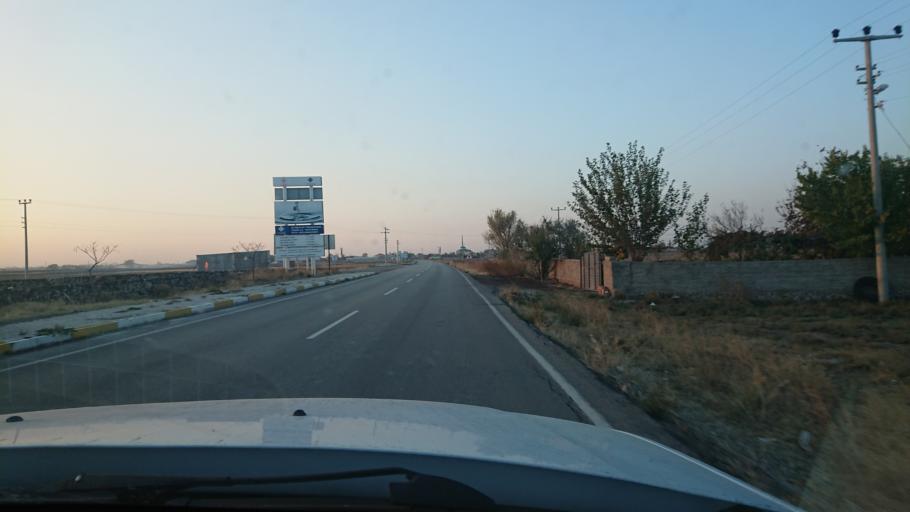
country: TR
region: Aksaray
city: Aksaray
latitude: 38.3130
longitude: 34.0609
